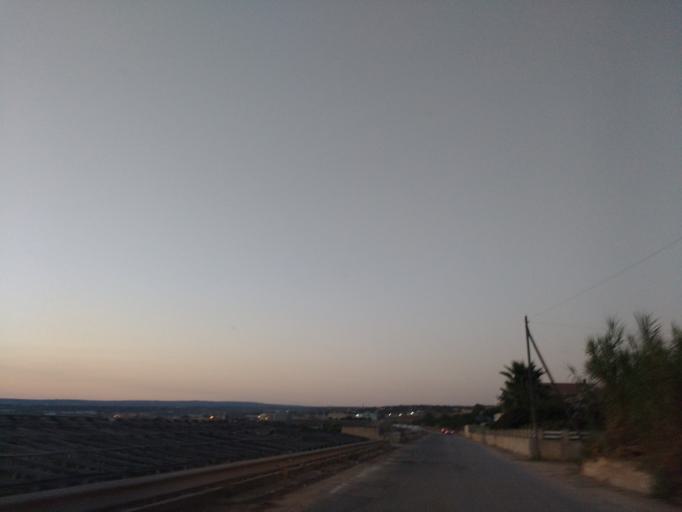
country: IT
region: Sicily
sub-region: Ragusa
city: Cava d'Aliga
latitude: 36.7379
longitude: 14.6820
